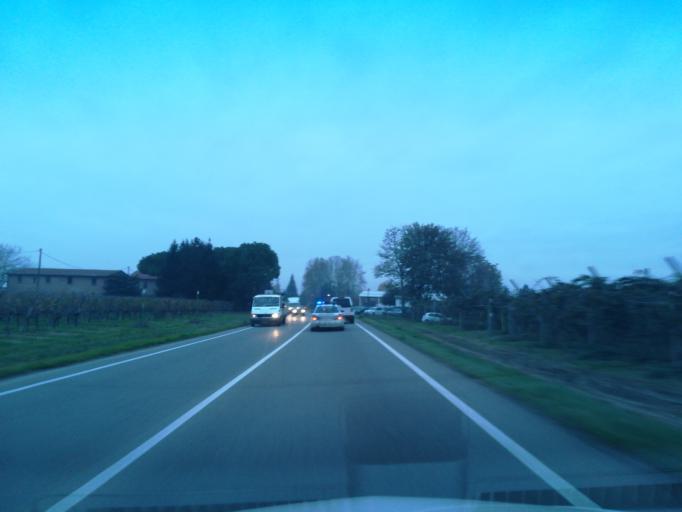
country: IT
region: Emilia-Romagna
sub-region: Provincia di Ravenna
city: Castel Bolognese
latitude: 44.3128
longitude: 11.8188
